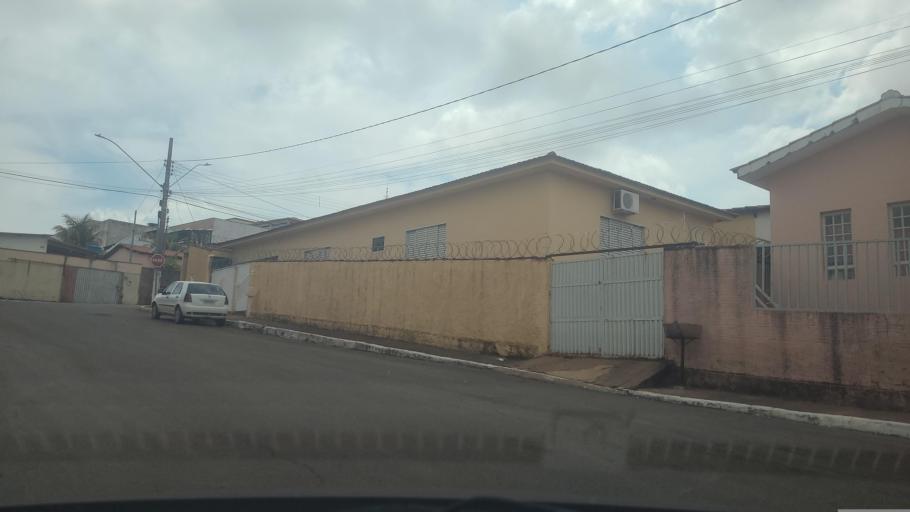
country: BR
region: Minas Gerais
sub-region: Carmo Do Paranaiba
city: Carmo do Paranaiba
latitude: -19.1959
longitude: -46.2446
